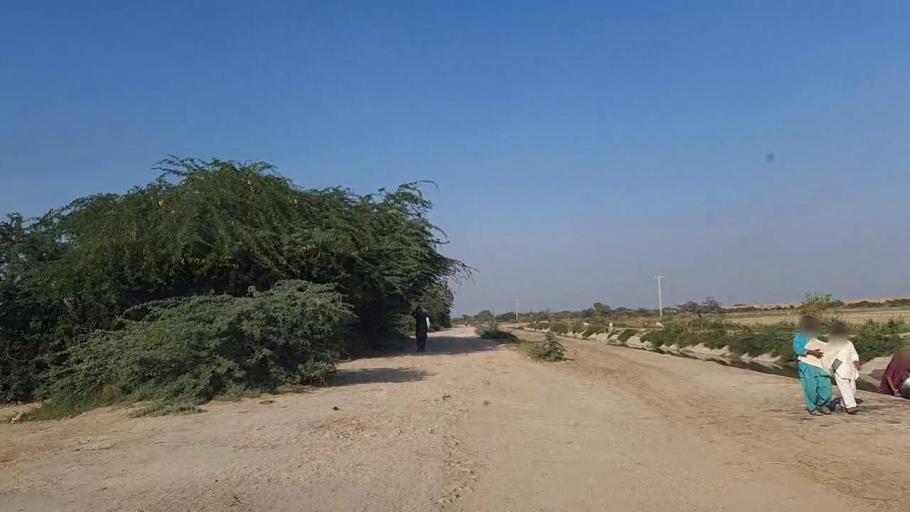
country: PK
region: Sindh
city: Thatta
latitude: 24.7411
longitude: 67.9678
